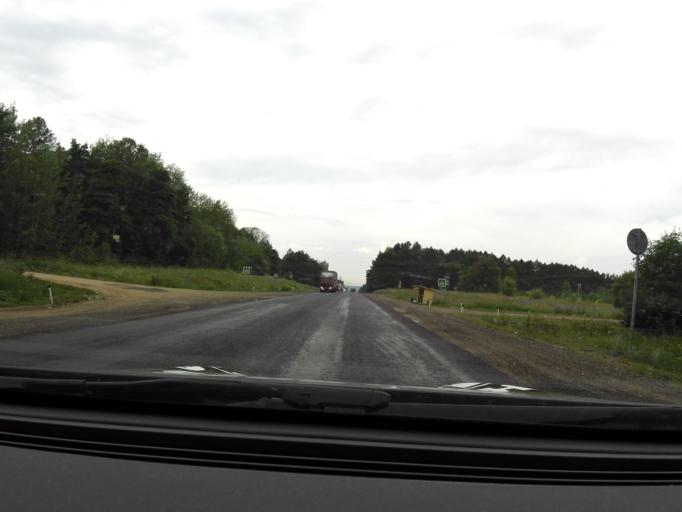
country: RU
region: Bashkortostan
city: Iglino
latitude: 54.7706
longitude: 56.4535
